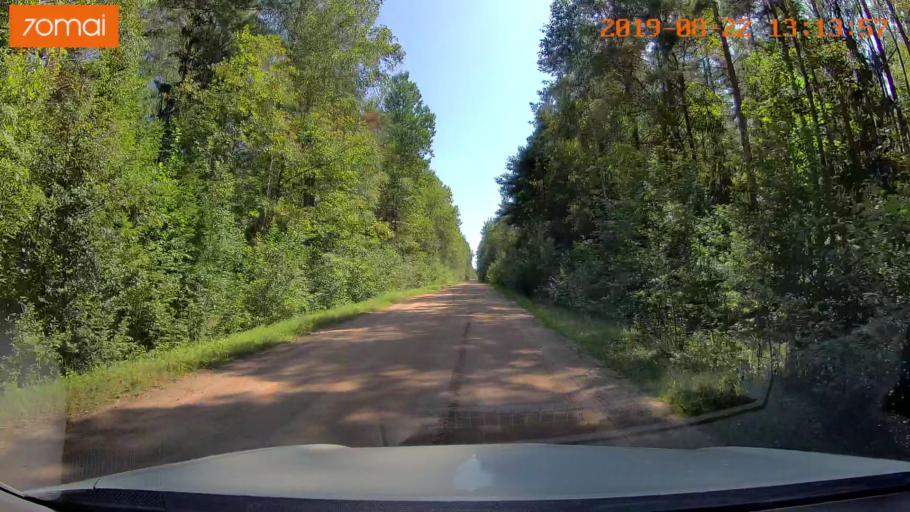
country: BY
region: Minsk
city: Prawdzinski
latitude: 53.2721
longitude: 27.8818
